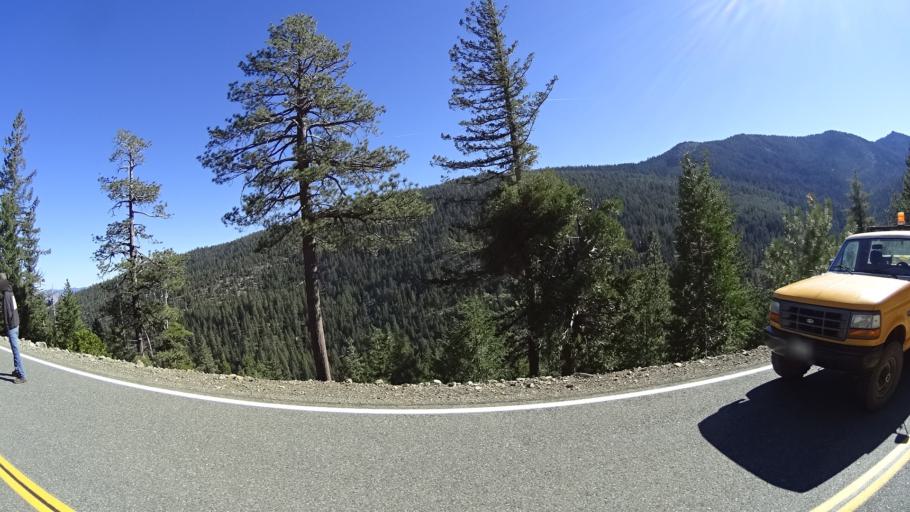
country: US
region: California
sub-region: Trinity County
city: Weaverville
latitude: 41.2365
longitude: -122.8925
